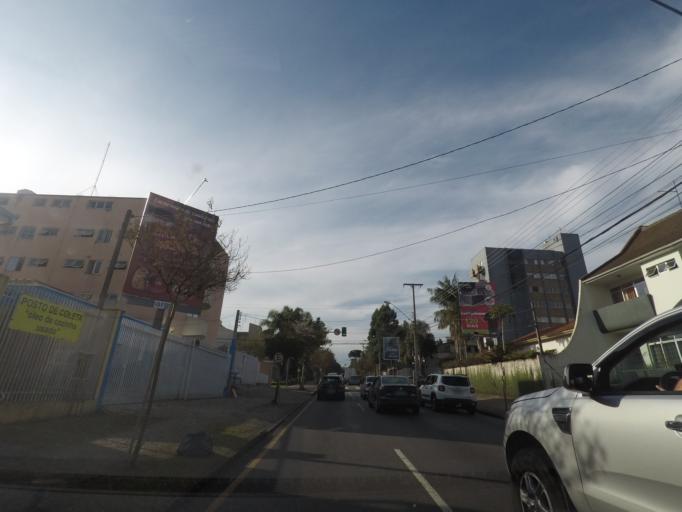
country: BR
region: Parana
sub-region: Curitiba
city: Curitiba
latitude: -25.4187
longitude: -49.2527
